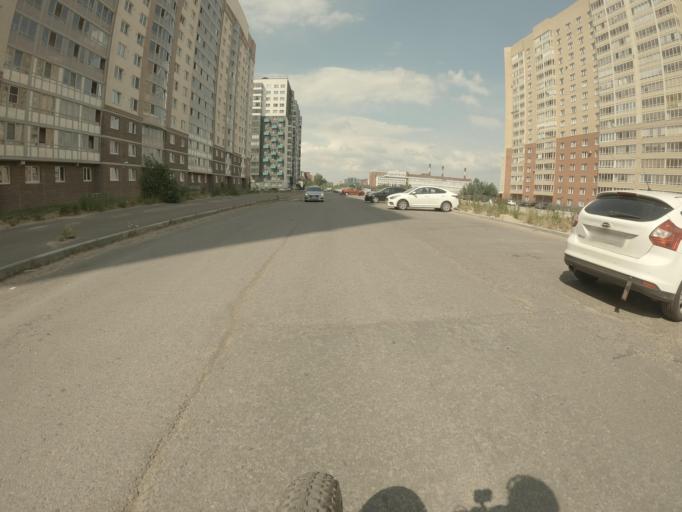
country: RU
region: St.-Petersburg
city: Krasnogvargeisky
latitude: 59.9183
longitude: 30.4400
